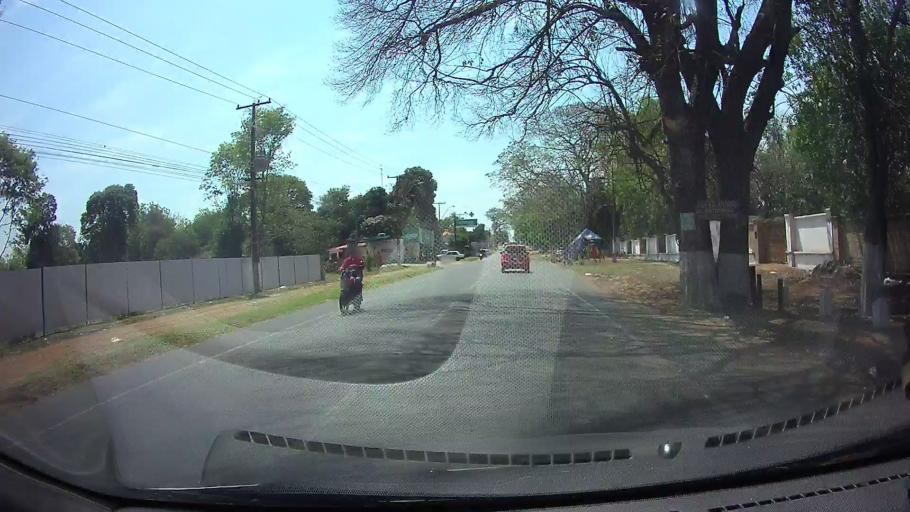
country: PY
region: Central
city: Capiata
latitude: -25.4150
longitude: -57.4574
